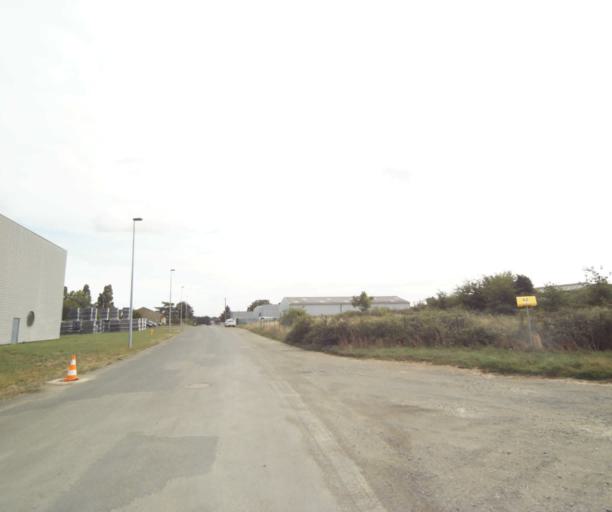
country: FR
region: Pays de la Loire
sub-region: Departement de la Sarthe
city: Sable-sur-Sarthe
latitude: 47.8213
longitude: -0.3080
